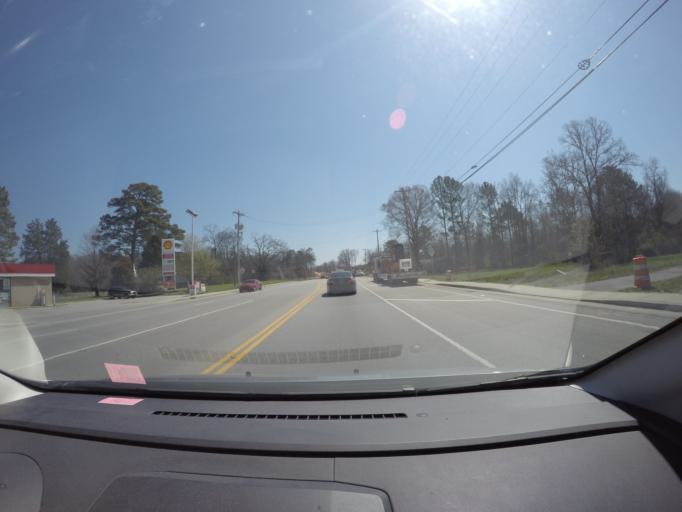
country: US
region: Tennessee
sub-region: Hamilton County
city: Collegedale
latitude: 35.0695
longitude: -85.1001
